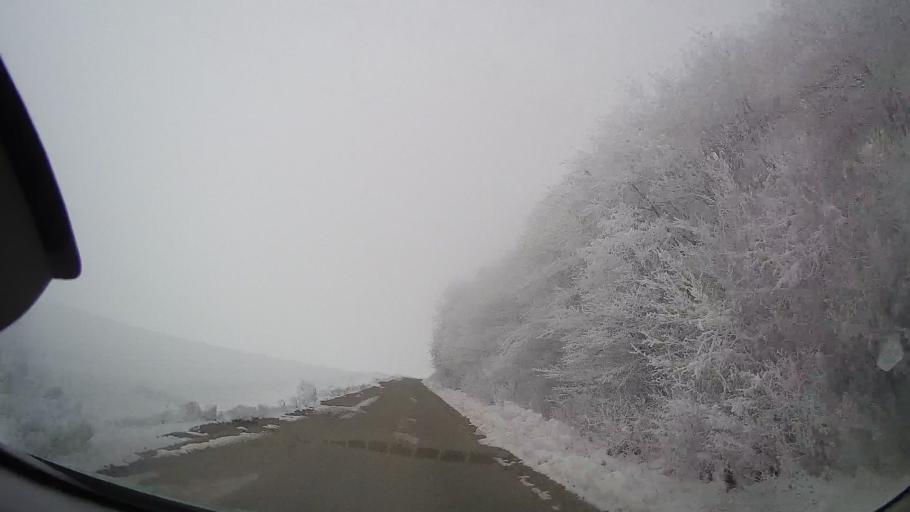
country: RO
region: Iasi
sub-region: Comuna Dagata
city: Dagata
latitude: 46.9096
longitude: 27.1849
